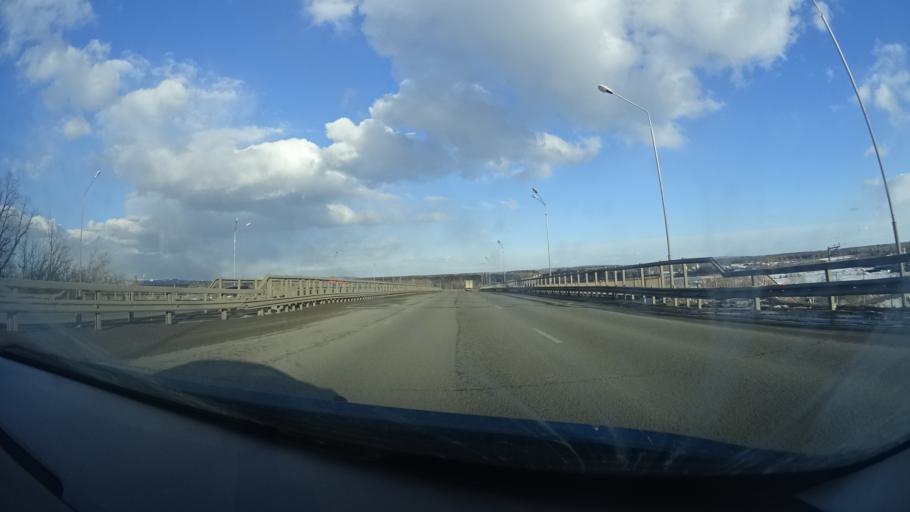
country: RU
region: Bashkortostan
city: Avdon
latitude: 54.6760
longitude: 55.8094
